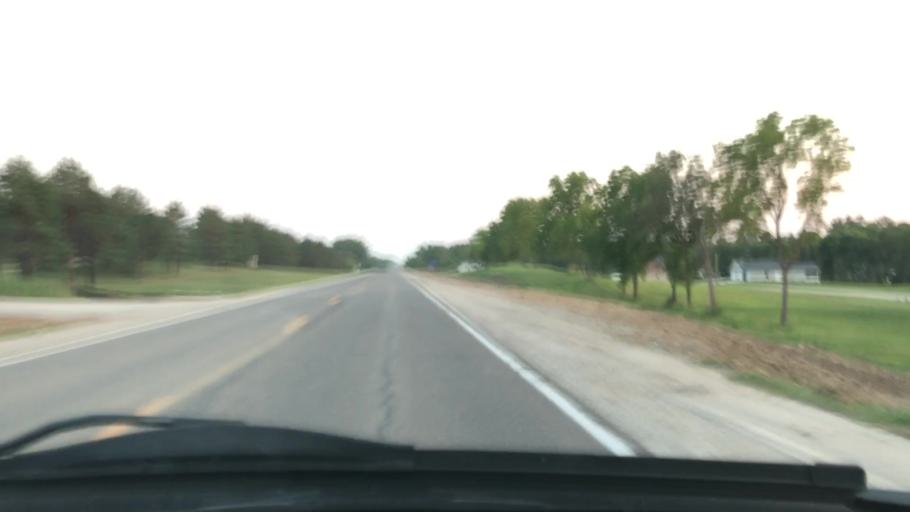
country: US
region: Iowa
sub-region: Henry County
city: Mount Pleasant
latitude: 40.9586
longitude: -91.5394
